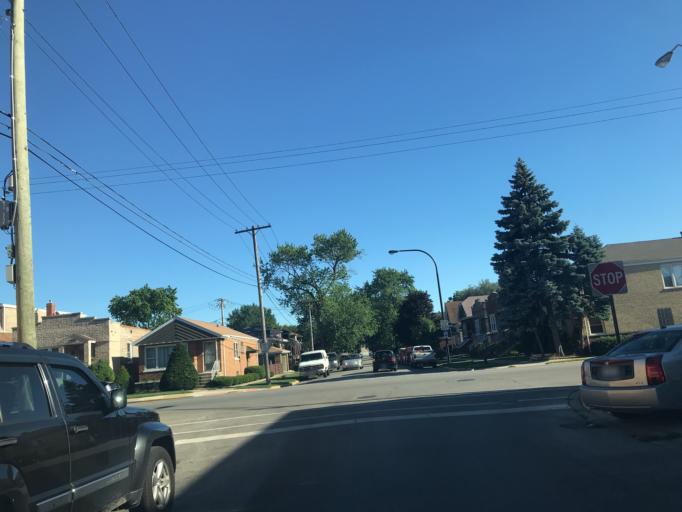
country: US
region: Illinois
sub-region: Cook County
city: Cicero
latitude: 41.8439
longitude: -87.7699
